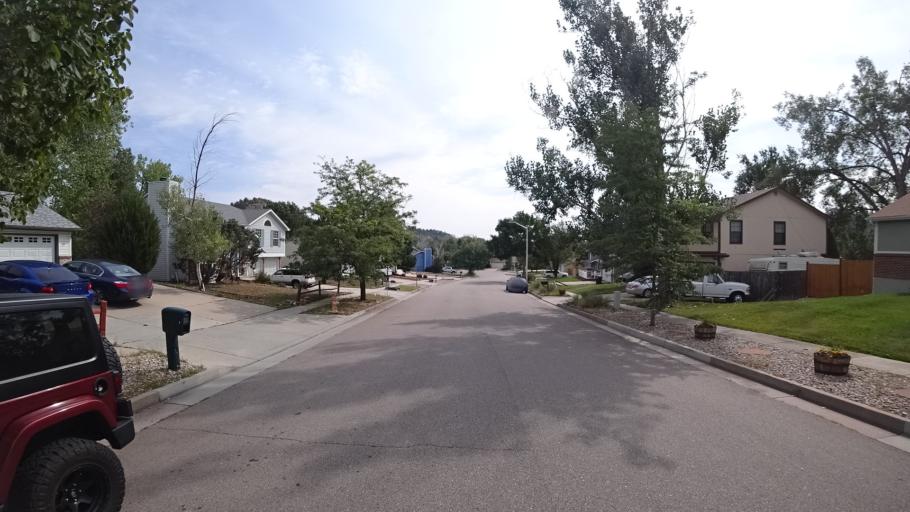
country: US
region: Colorado
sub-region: El Paso County
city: Colorado Springs
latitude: 38.8902
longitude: -104.7879
